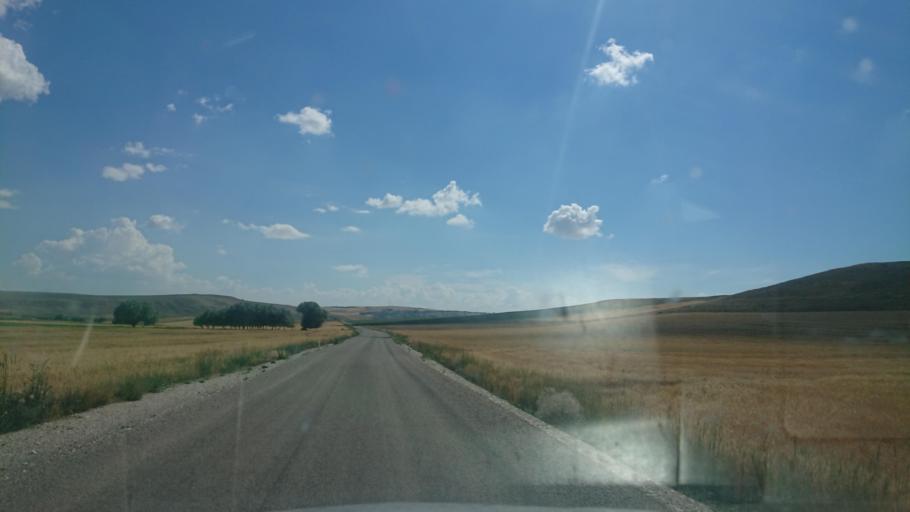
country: TR
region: Aksaray
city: Agacoren
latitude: 38.7947
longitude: 33.8181
